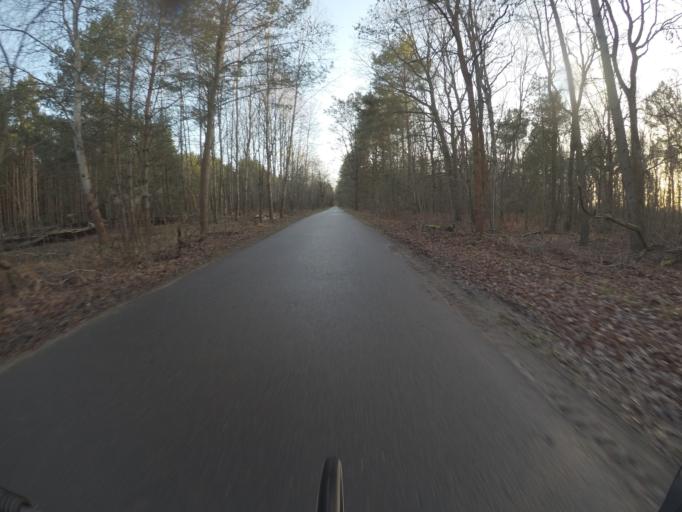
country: DE
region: Brandenburg
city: Hennigsdorf
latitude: 52.6528
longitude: 13.2231
